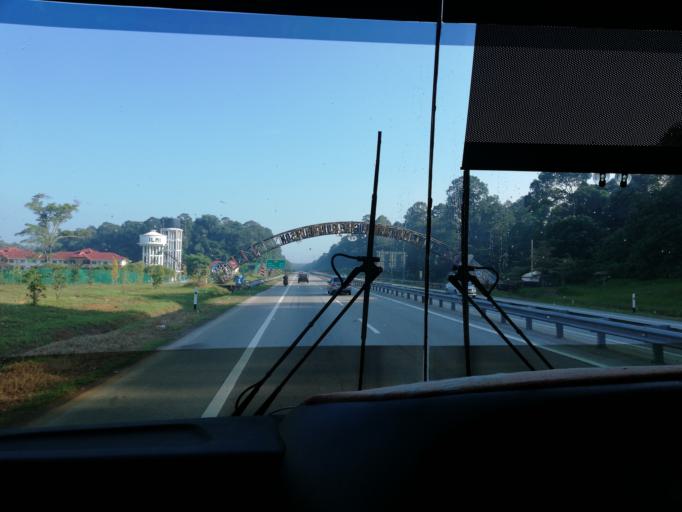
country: MY
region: Negeri Sembilan
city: Port Dickson
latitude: 2.5035
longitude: 101.8653
